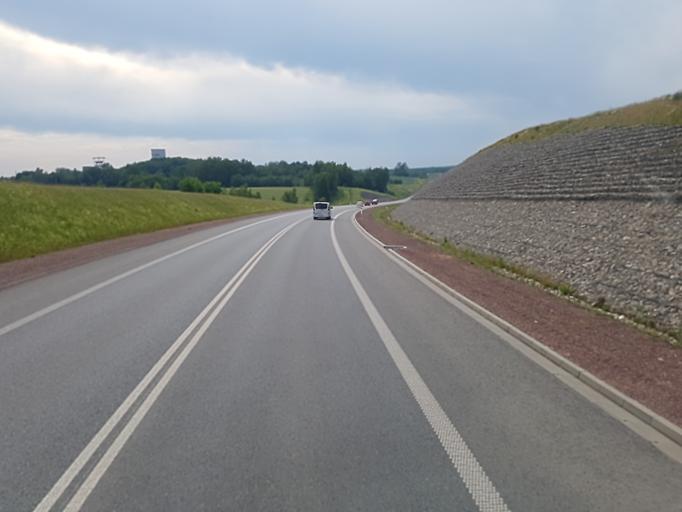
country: PL
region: Silesian Voivodeship
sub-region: Jastrzebie-Zdroj
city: Jastrzebie Zdroj
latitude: 49.9725
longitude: 18.5792
